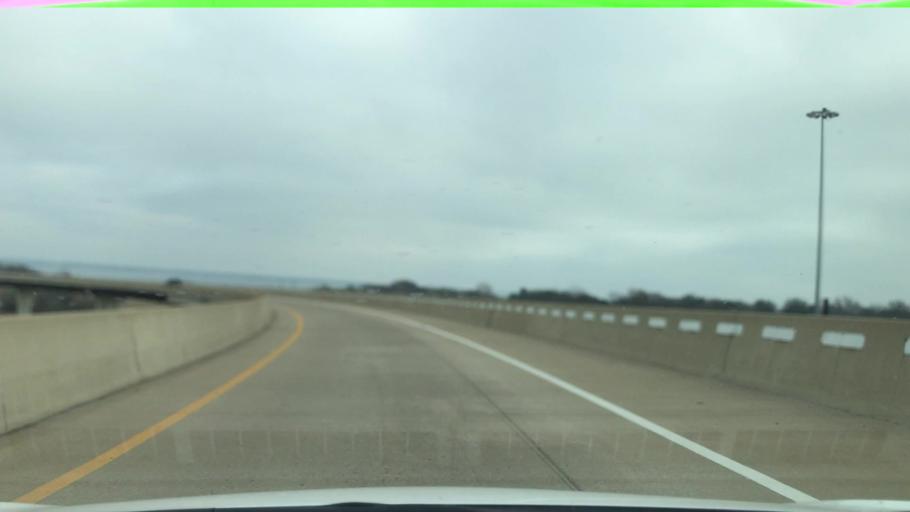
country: US
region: Texas
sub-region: Dallas County
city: Rowlett
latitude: 32.8593
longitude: -96.5541
